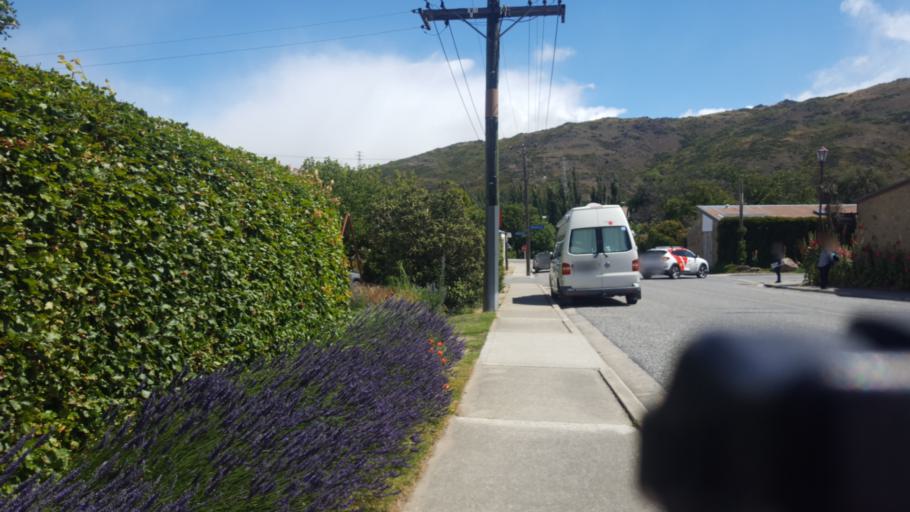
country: NZ
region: Otago
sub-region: Queenstown-Lakes District
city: Wanaka
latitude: -45.1864
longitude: 169.3177
